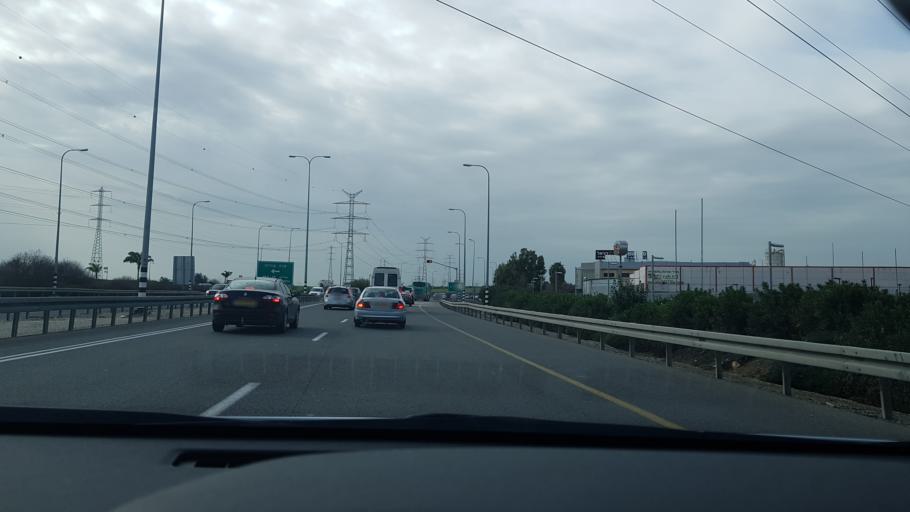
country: IL
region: Southern District
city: Ashdod
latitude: 31.7630
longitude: 34.6673
